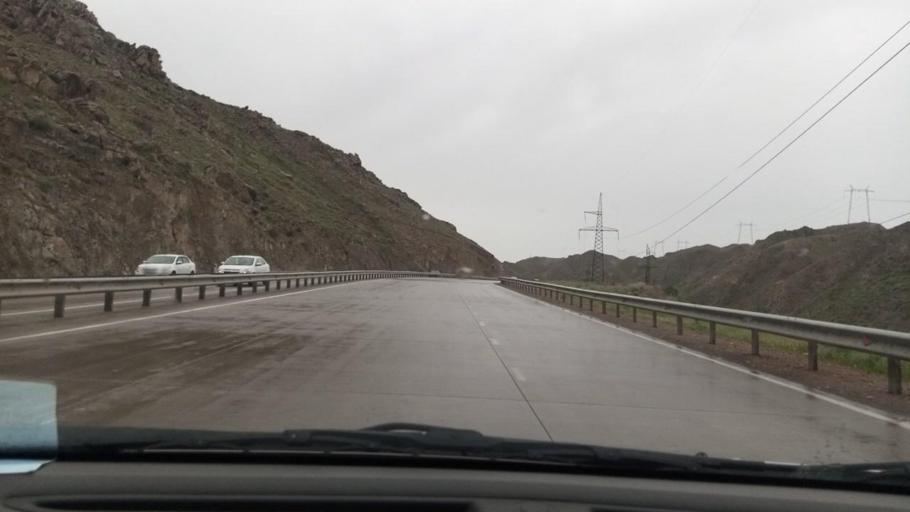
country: TJ
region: Viloyati Sughd
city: Shaydon
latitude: 40.9737
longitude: 70.6524
